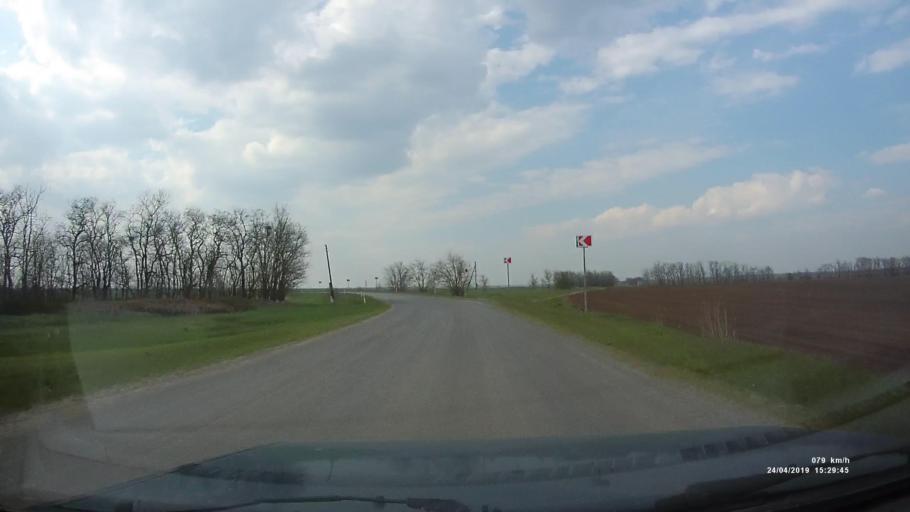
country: RU
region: Rostov
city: Remontnoye
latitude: 46.5975
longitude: 43.0166
